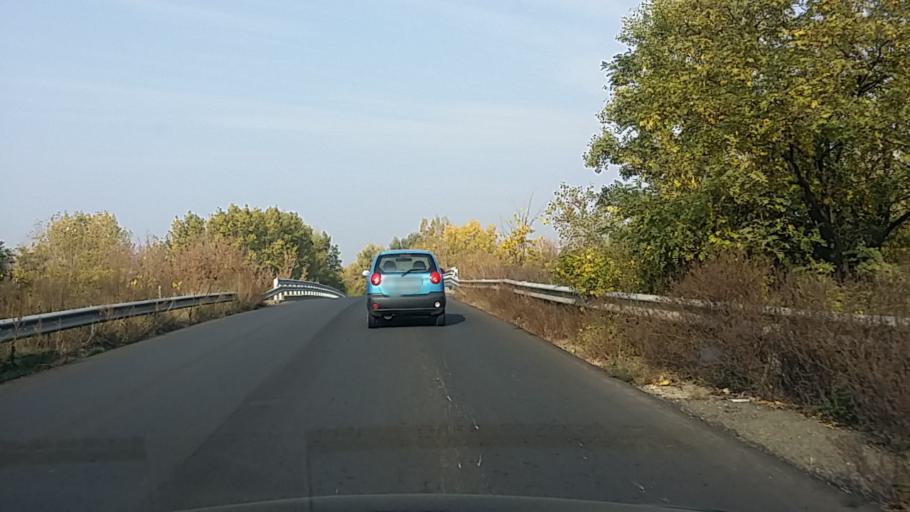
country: HU
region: Pest
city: Dunakeszi
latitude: 47.6001
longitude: 19.1524
